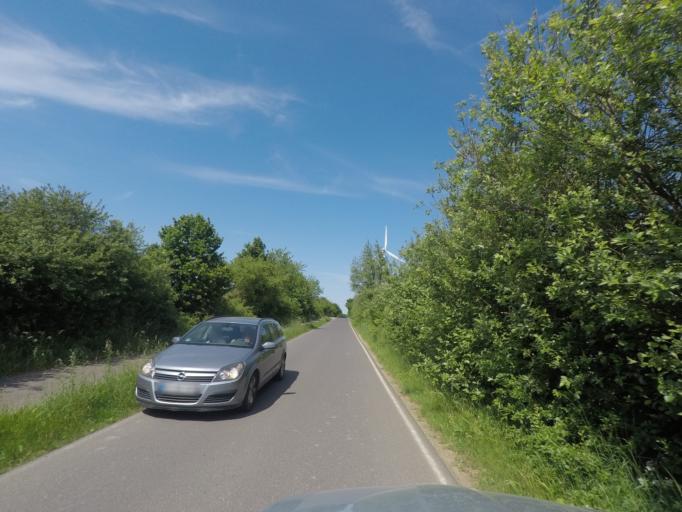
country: DE
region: Brandenburg
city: Britz
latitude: 52.8744
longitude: 13.7638
